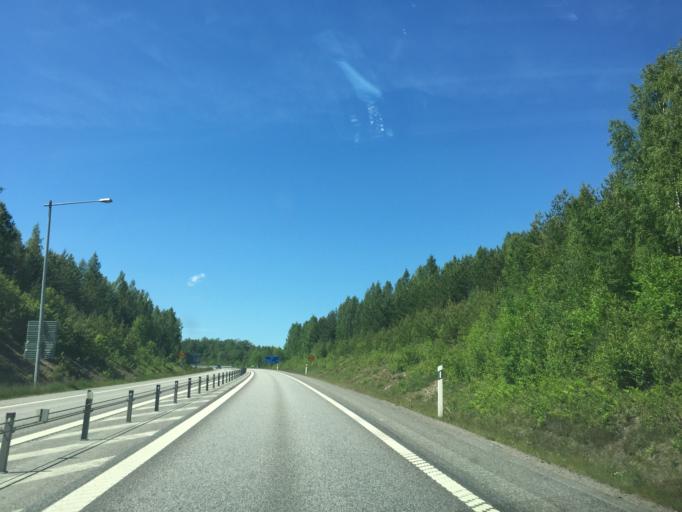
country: SE
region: OEstergoetland
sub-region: Motala Kommun
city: Motala
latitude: 58.6291
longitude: 14.9754
